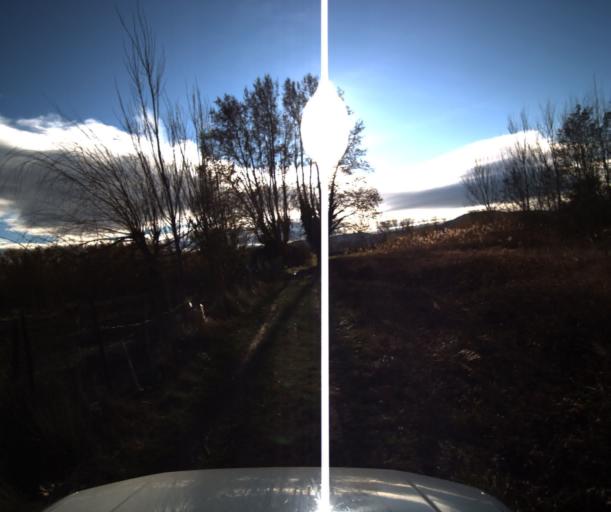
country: FR
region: Provence-Alpes-Cote d'Azur
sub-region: Departement du Vaucluse
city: Pertuis
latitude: 43.6776
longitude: 5.4775
